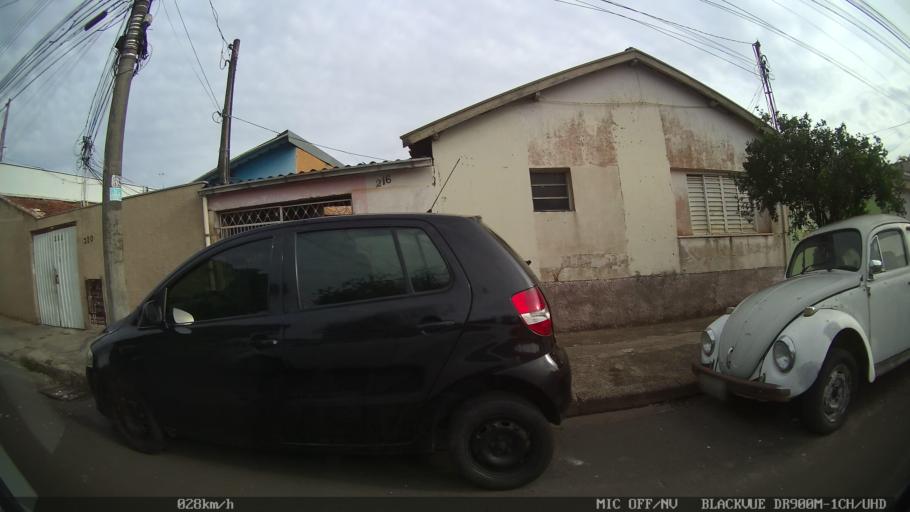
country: BR
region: Sao Paulo
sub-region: Piracicaba
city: Piracicaba
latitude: -22.7328
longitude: -47.6268
